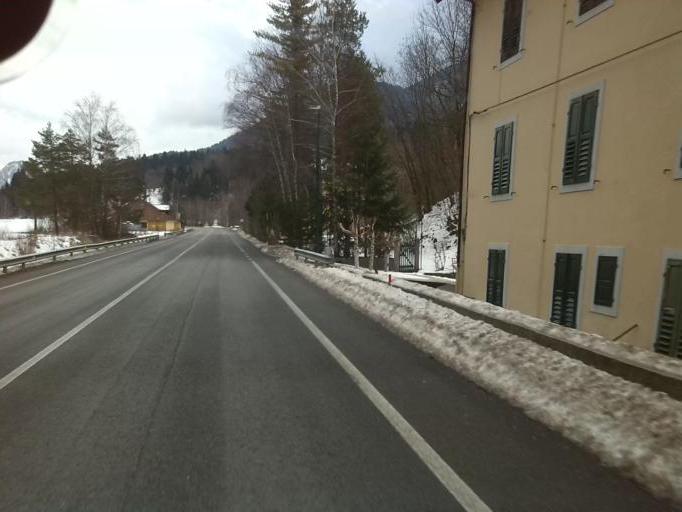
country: IT
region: Friuli Venezia Giulia
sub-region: Provincia di Udine
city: Malborghetto
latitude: 46.5010
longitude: 13.3952
